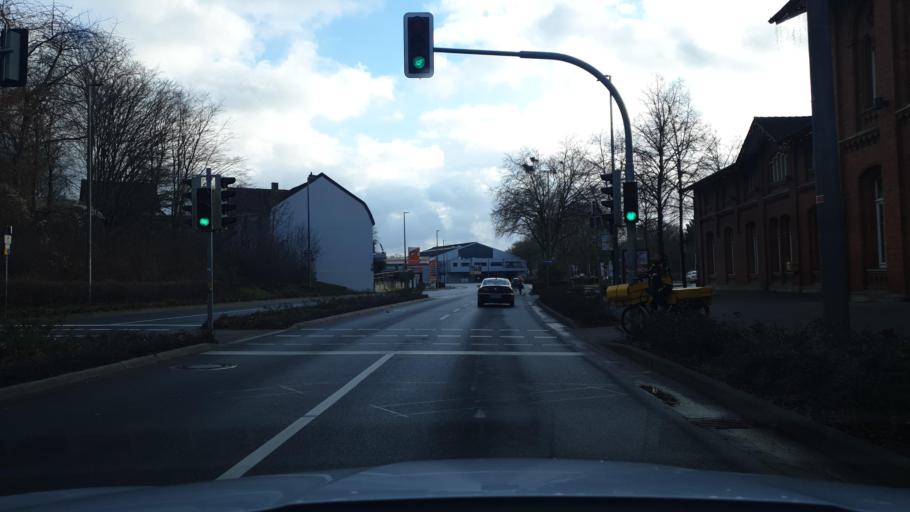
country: DE
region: North Rhine-Westphalia
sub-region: Regierungsbezirk Detmold
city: Bad Salzuflen
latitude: 52.0820
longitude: 8.7406
